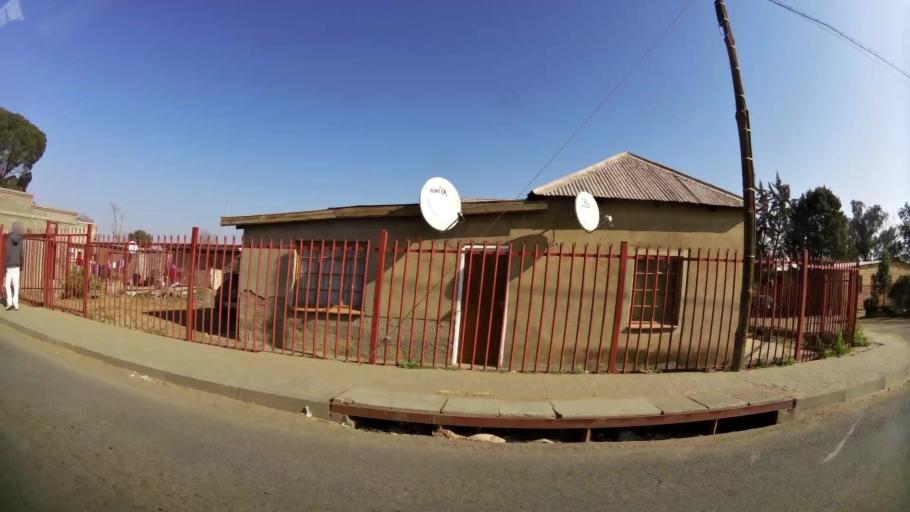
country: ZA
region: Orange Free State
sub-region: Mangaung Metropolitan Municipality
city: Bloemfontein
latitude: -29.1380
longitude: 26.2379
